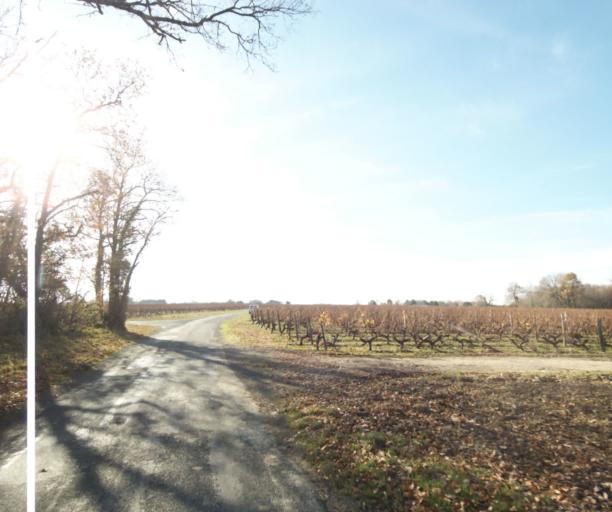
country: FR
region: Poitou-Charentes
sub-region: Departement de la Charente-Maritime
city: Chaniers
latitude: 45.7561
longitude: -0.5124
